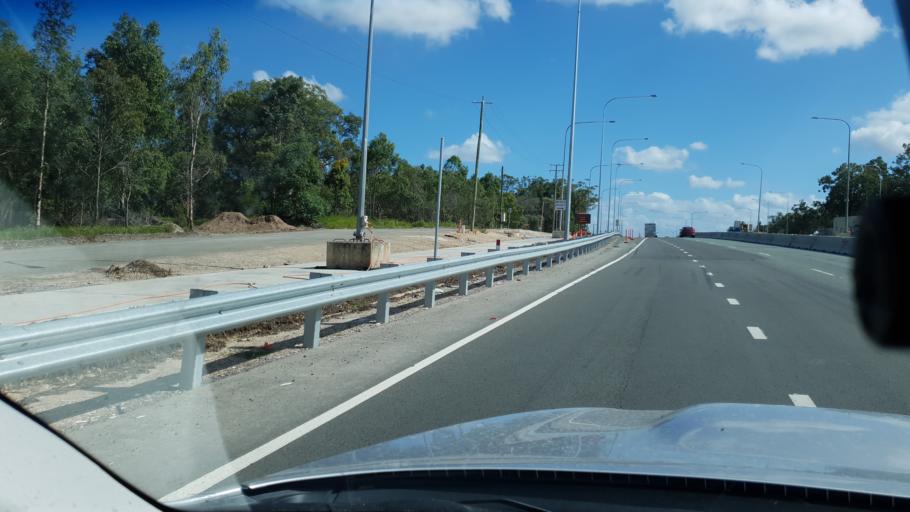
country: AU
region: Queensland
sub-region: Brisbane
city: Sunnybank Hills
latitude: -27.6494
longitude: 153.0411
